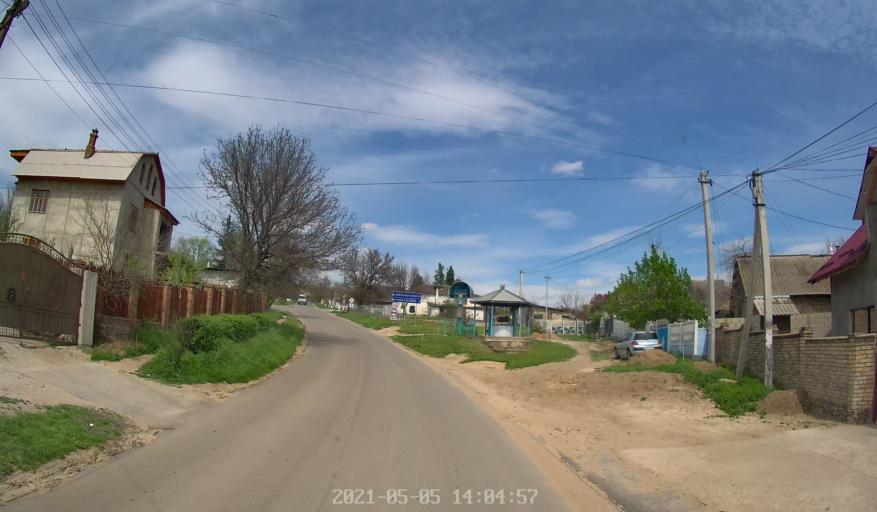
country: MD
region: Chisinau
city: Vadul lui Voda
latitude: 47.0655
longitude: 29.1321
